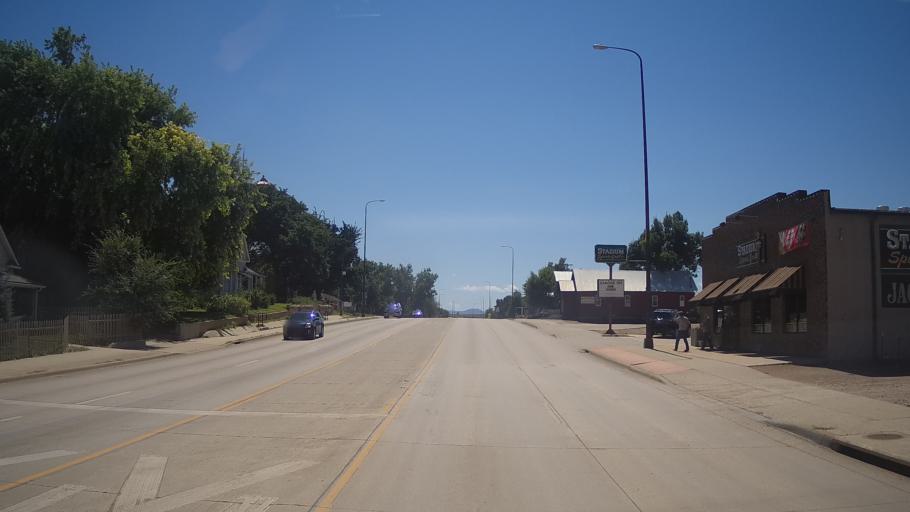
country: US
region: South Dakota
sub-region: Butte County
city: Belle Fourche
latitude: 44.6698
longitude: -103.8536
